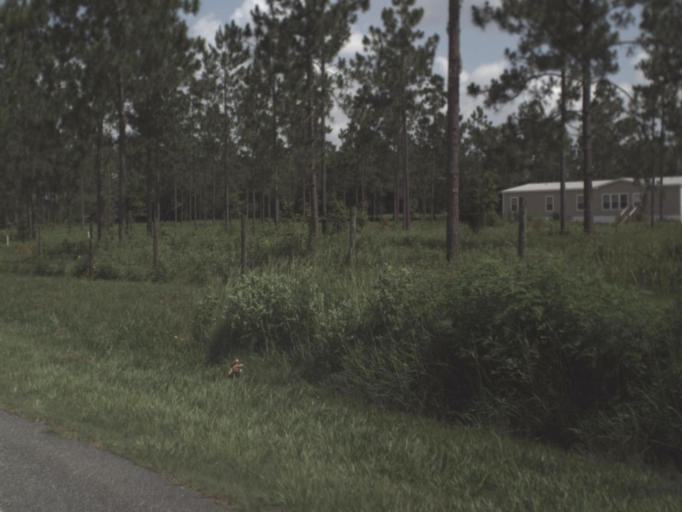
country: US
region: Florida
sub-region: Madison County
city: Madison
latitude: 30.4410
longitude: -83.3285
